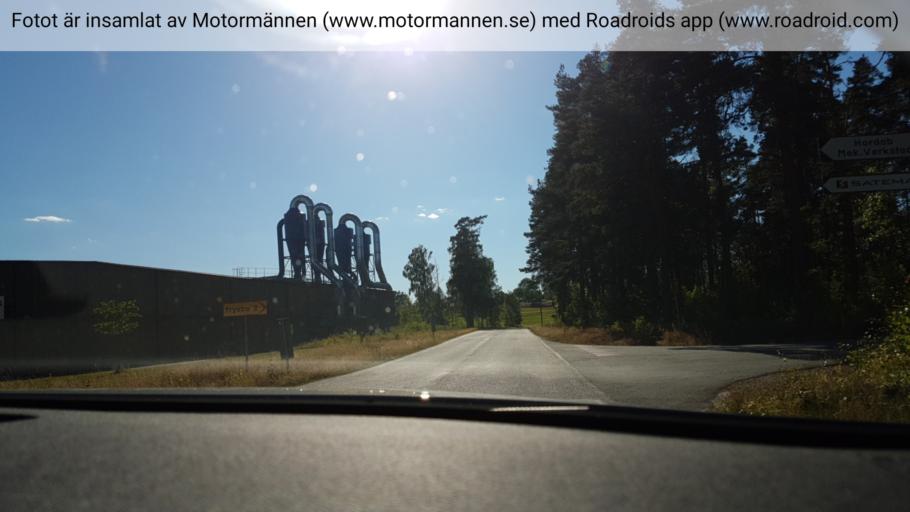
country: SE
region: Joenkoeping
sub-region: Vaggeryds Kommun
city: Skillingaryd
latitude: 57.3537
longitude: 14.0962
